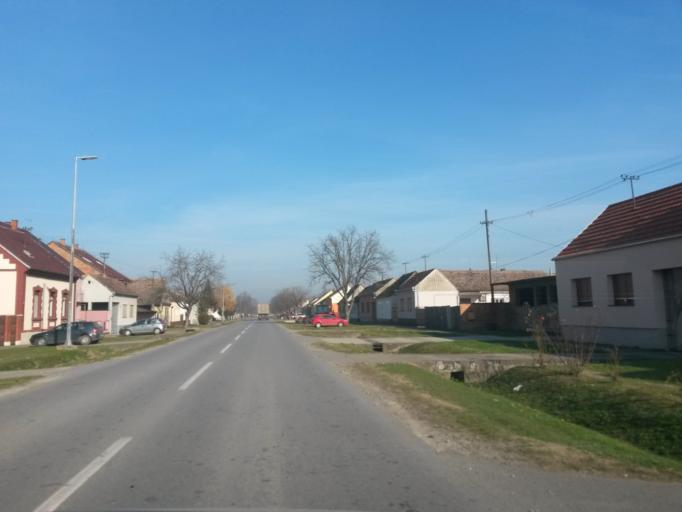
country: HR
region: Vukovarsko-Srijemska
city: Privlaka
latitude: 45.1966
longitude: 18.8405
